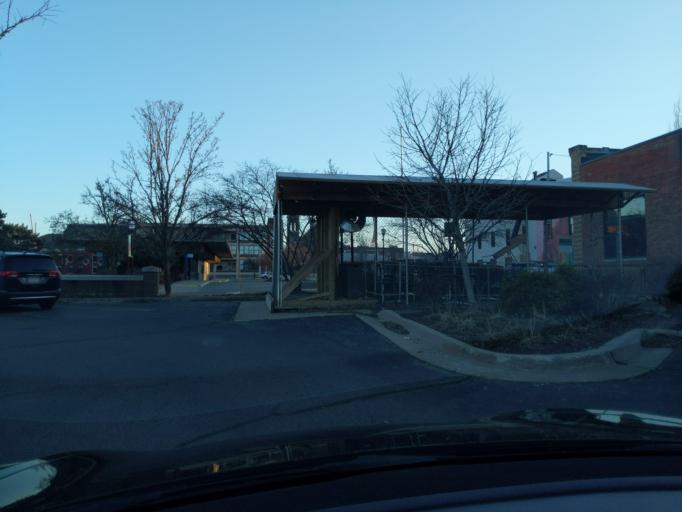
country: US
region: Michigan
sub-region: Jackson County
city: Jackson
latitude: 42.2468
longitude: -84.4069
